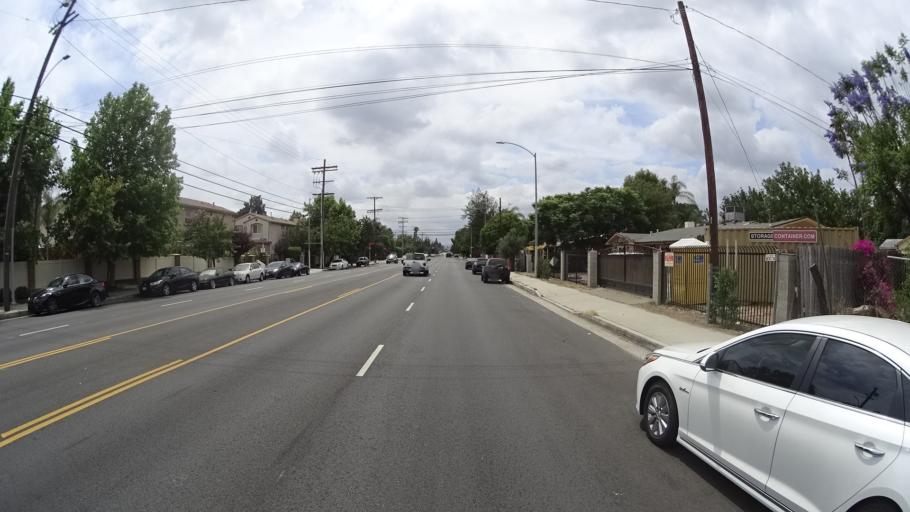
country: US
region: California
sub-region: Los Angeles County
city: San Fernando
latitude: 34.2428
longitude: -118.4575
